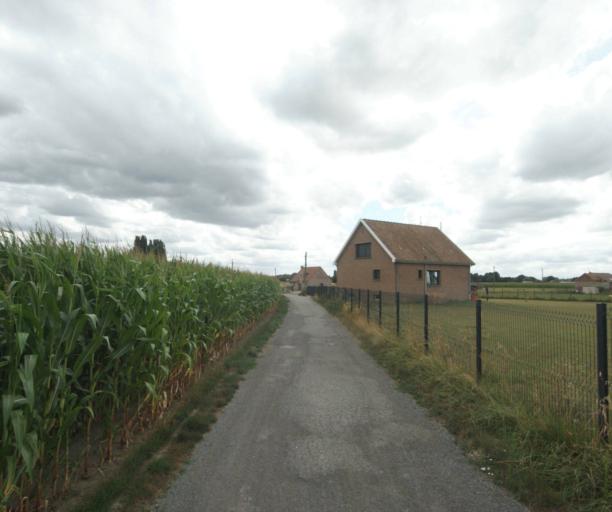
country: FR
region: Nord-Pas-de-Calais
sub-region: Departement du Nord
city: Linselles
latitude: 50.7501
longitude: 3.0711
